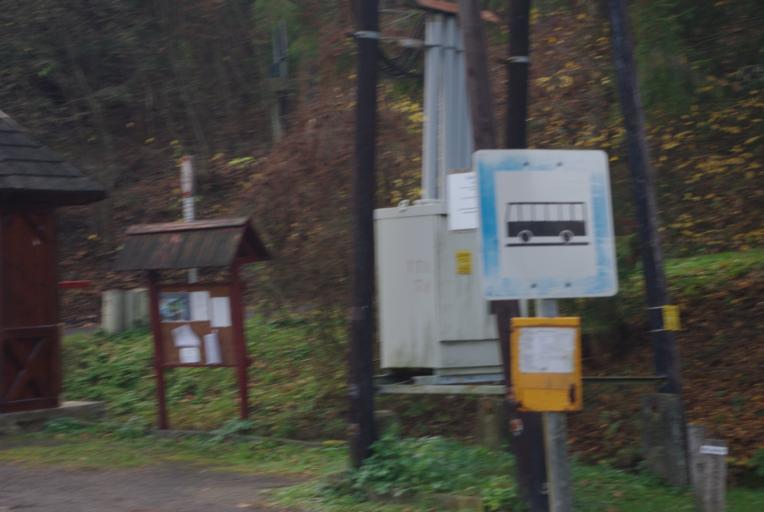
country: HU
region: Borsod-Abauj-Zemplen
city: Sarospatak
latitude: 48.4232
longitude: 21.5385
